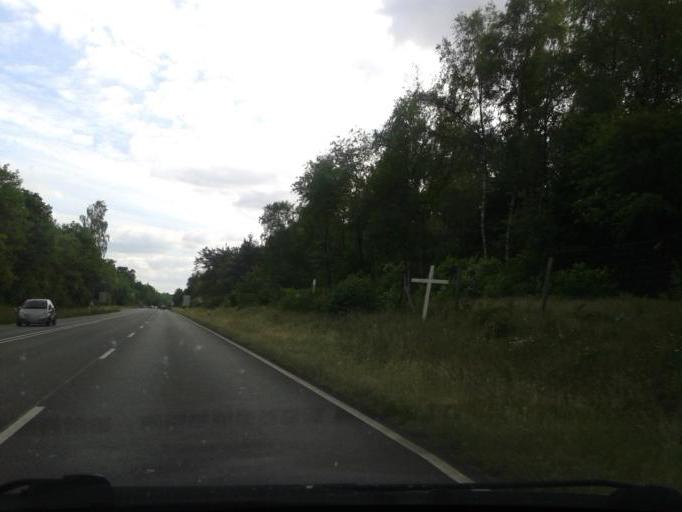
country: DE
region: North Rhine-Westphalia
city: Bad Lippspringe
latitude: 51.7734
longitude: 8.7756
